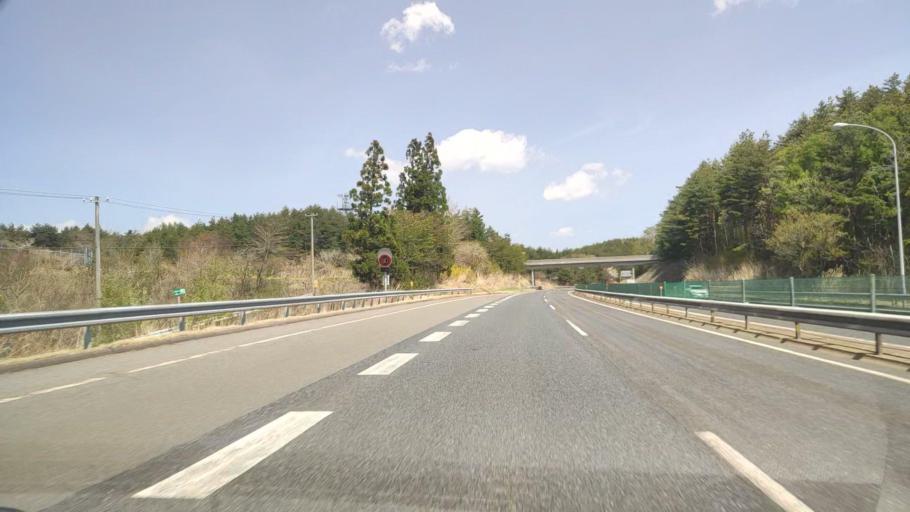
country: JP
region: Iwate
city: Ichinohe
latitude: 40.2997
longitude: 141.4231
